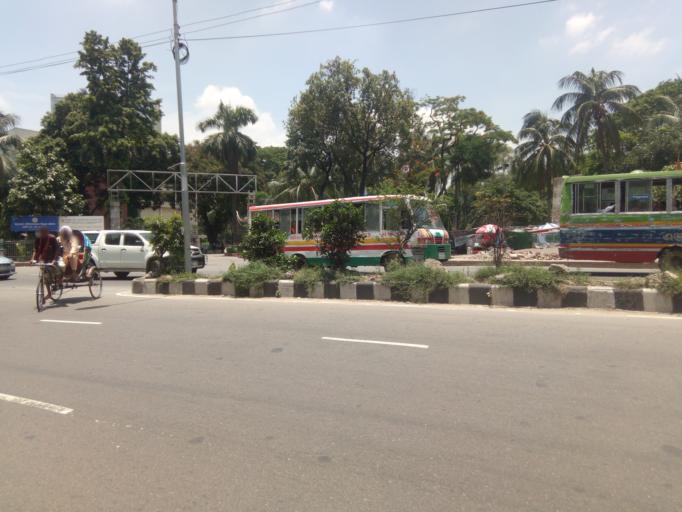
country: BD
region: Dhaka
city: Paltan
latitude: 23.7347
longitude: 90.4009
